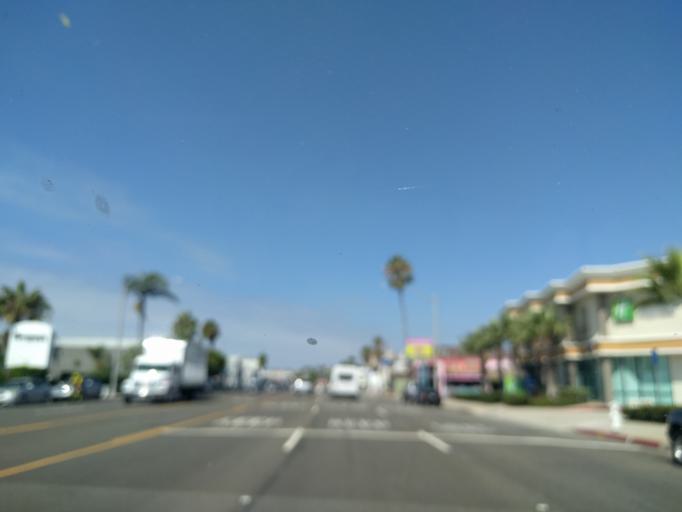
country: US
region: California
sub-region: Orange County
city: Newport Beach
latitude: 33.6187
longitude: -117.9207
